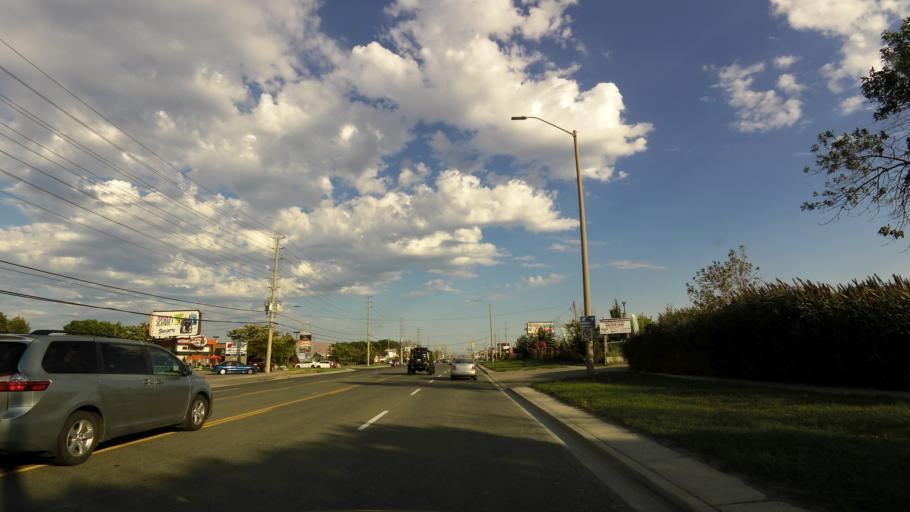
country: CA
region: Ontario
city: Mississauga
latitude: 43.5763
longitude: -79.6478
